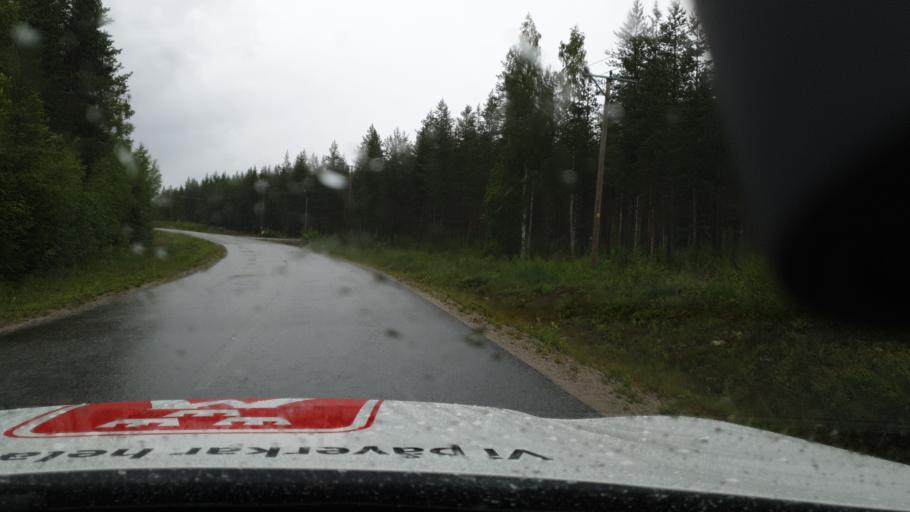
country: SE
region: Vaesterbotten
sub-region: Vindelns Kommun
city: Vindeln
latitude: 64.3917
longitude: 19.6762
